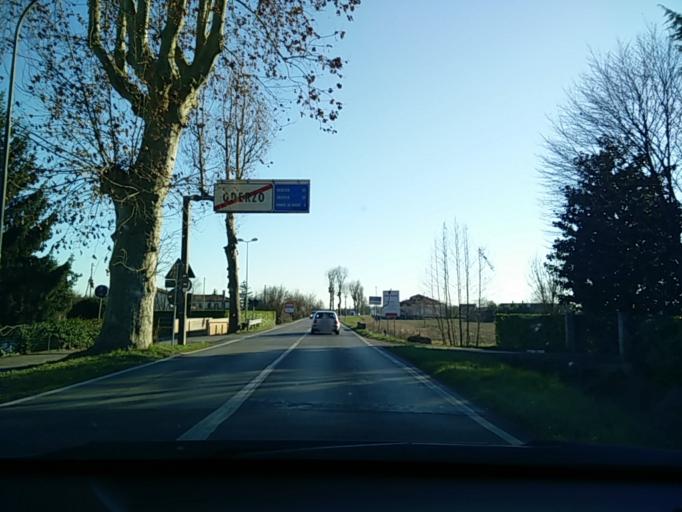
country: IT
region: Veneto
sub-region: Provincia di Treviso
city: Oderzo
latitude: 45.7673
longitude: 12.4872
